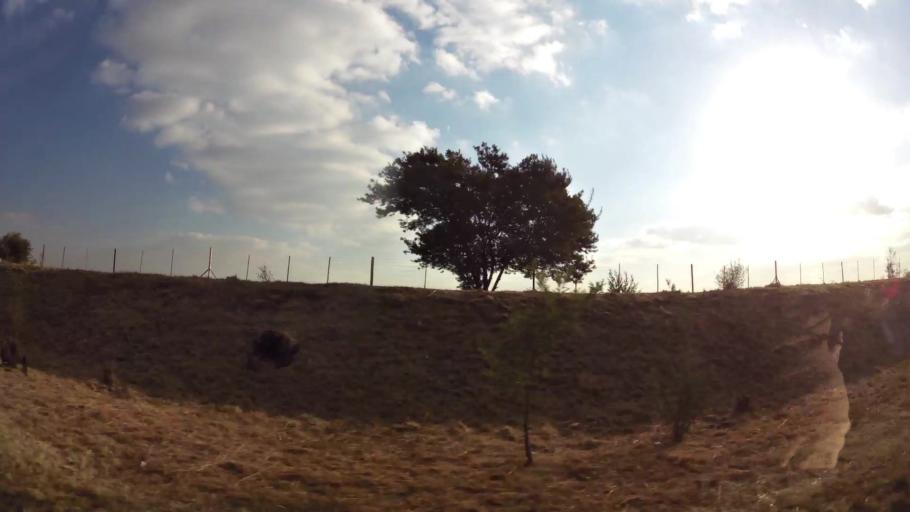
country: ZA
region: Gauteng
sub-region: West Rand District Municipality
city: Krugersdorp
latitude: -26.0968
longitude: 27.7328
